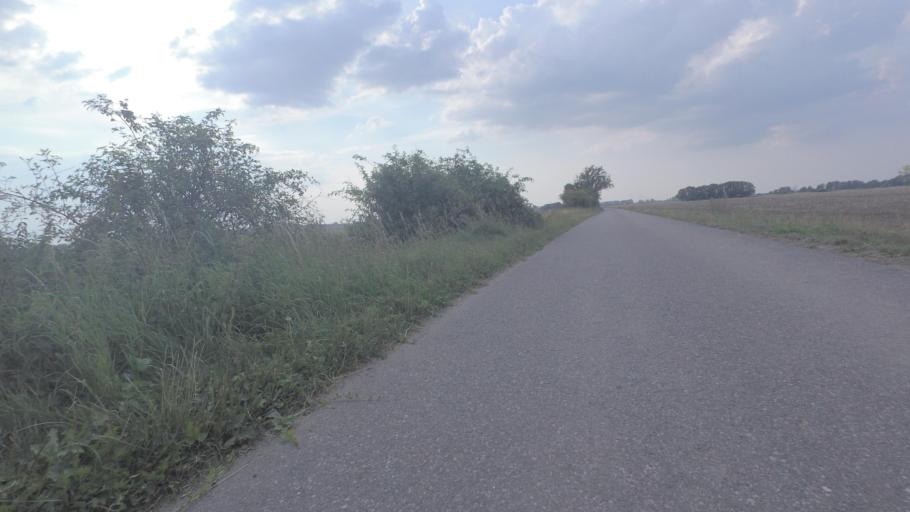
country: DE
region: Brandenburg
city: Wittstock
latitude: 53.2405
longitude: 12.4606
